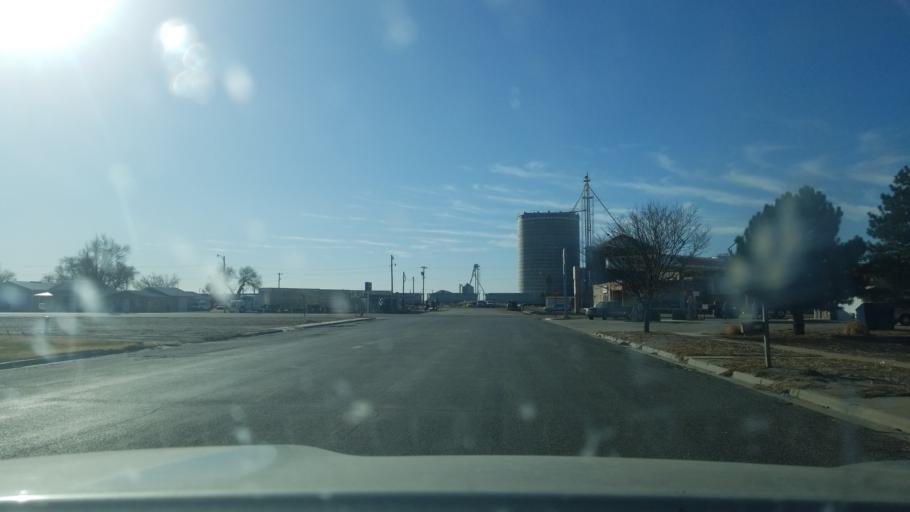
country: US
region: Kansas
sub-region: Ness County
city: Ness City
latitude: 38.4535
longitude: -99.8996
